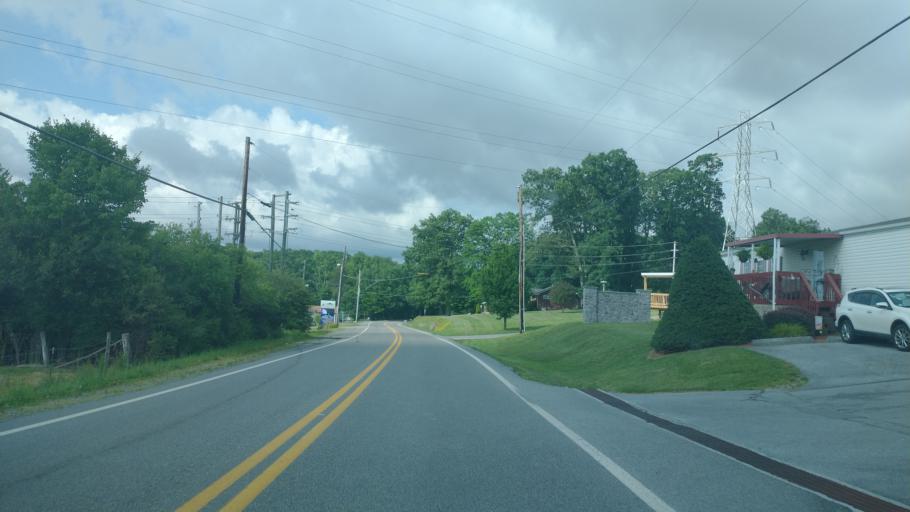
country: US
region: West Virginia
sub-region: Mercer County
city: Princeton
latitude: 37.3540
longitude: -81.1496
